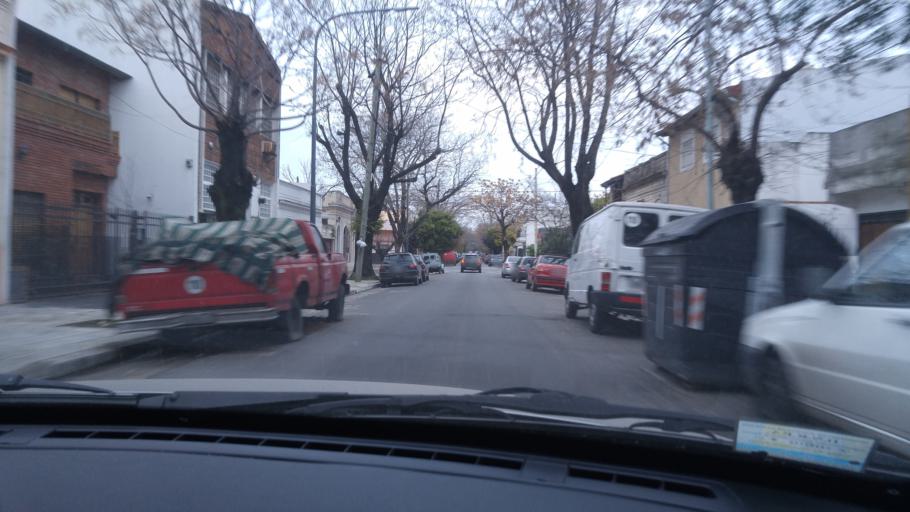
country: AR
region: Buenos Aires F.D.
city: Villa Santa Rita
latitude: -34.6297
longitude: -58.5116
